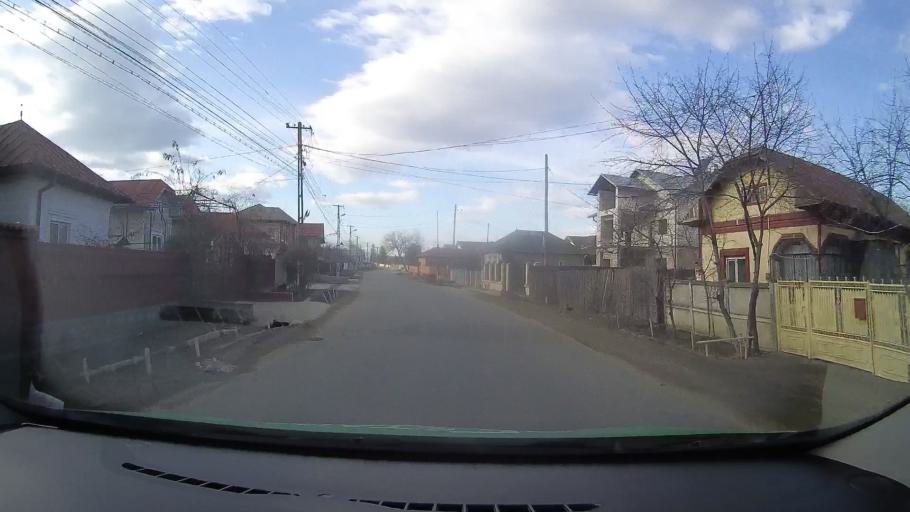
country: RO
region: Dambovita
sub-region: Comuna Ulmi
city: Ulmi
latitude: 44.8864
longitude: 25.5101
